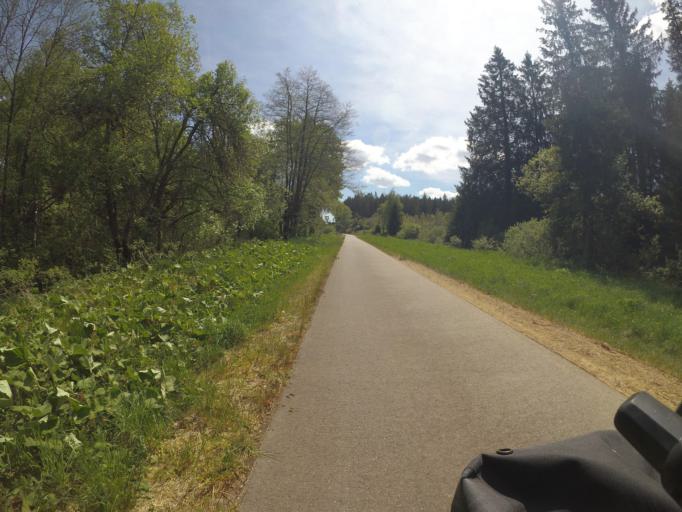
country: BE
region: Wallonia
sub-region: Province de Liege
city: Bullange
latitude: 50.3726
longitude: 6.3237
